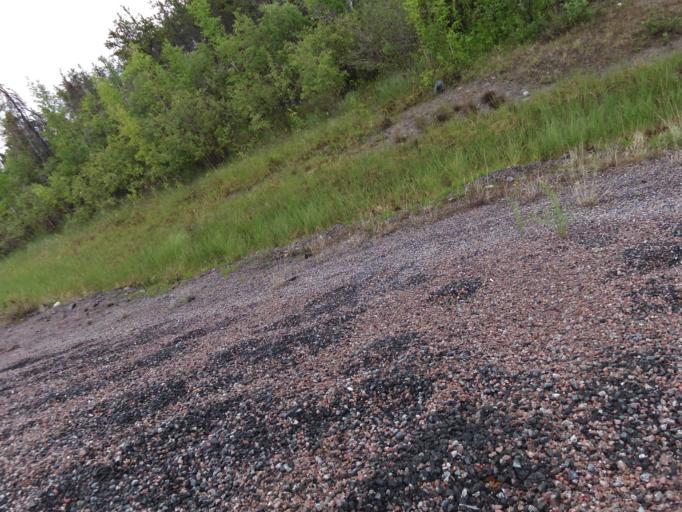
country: CA
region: Northwest Territories
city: Yellowknife
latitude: 62.4607
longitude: -114.3756
